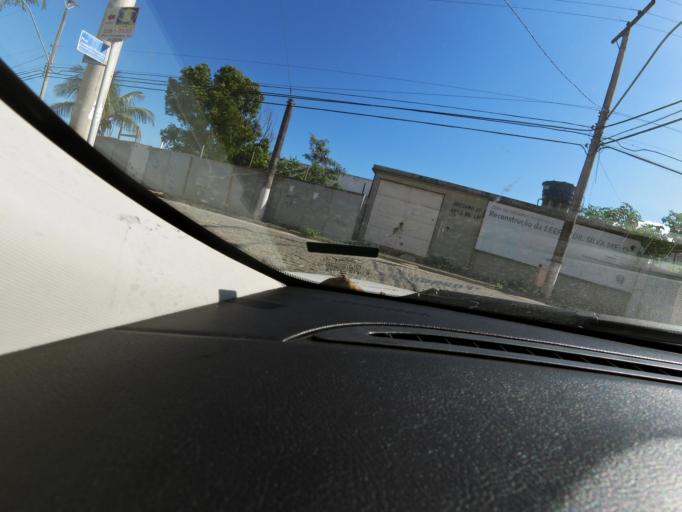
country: BR
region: Espirito Santo
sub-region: Guarapari
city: Guarapari
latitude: -20.6611
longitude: -40.5041
